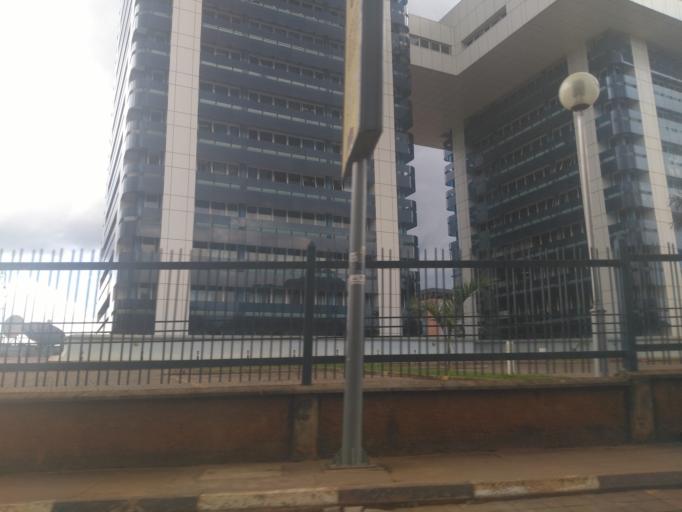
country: UG
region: Central Region
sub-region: Kampala District
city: Kampala
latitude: 0.3180
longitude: 32.5883
